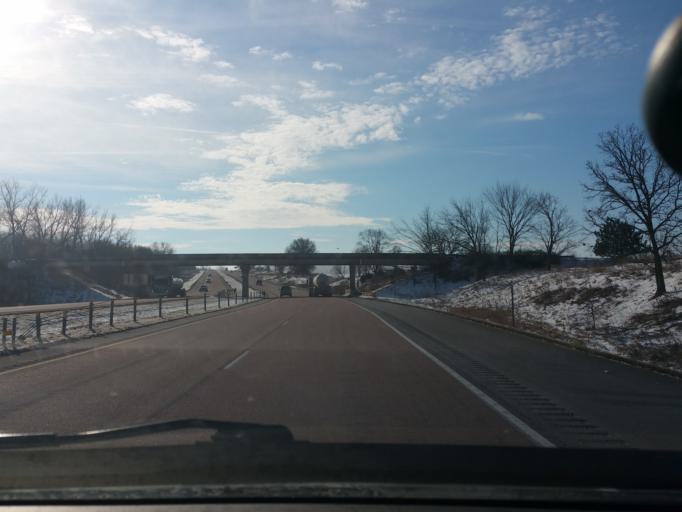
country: US
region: Iowa
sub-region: Warren County
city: Norwalk
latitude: 41.3238
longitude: -93.7803
